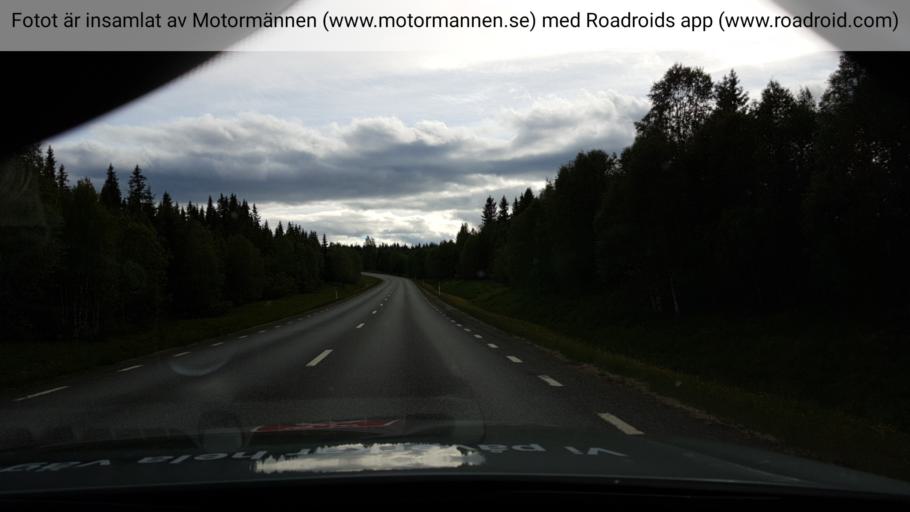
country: SE
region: Jaemtland
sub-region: OEstersunds Kommun
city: Lit
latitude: 63.4717
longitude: 15.1979
